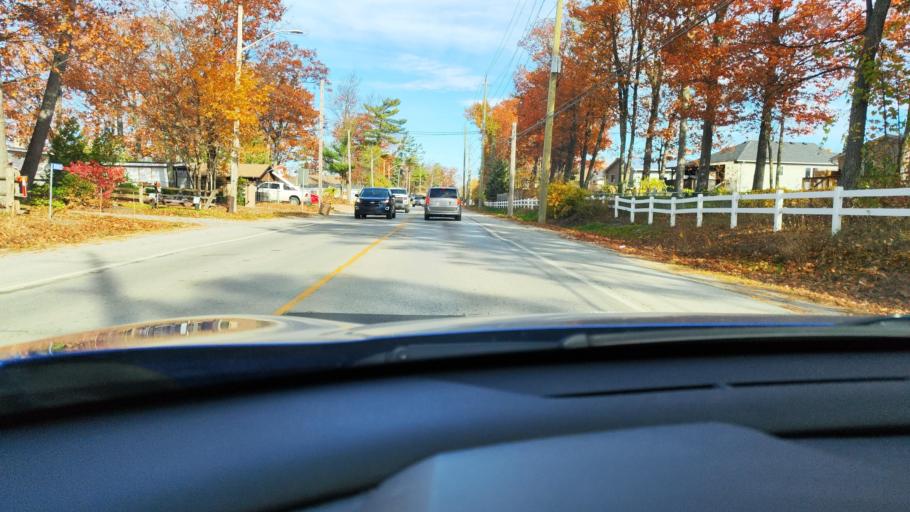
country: CA
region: Ontario
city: Wasaga Beach
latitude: 44.5158
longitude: -80.0218
